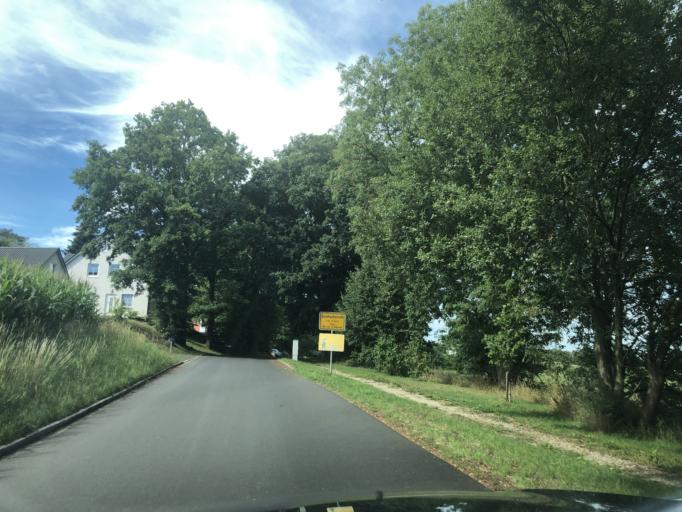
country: DE
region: Bavaria
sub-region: Upper Palatinate
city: Trabitz
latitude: 49.7972
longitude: 11.8811
